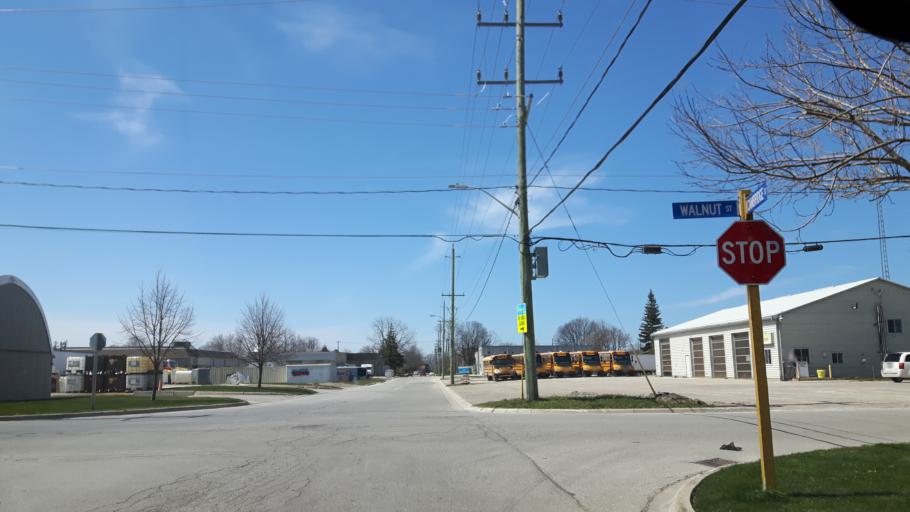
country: CA
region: Ontario
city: Goderich
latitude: 43.7367
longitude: -81.6972
